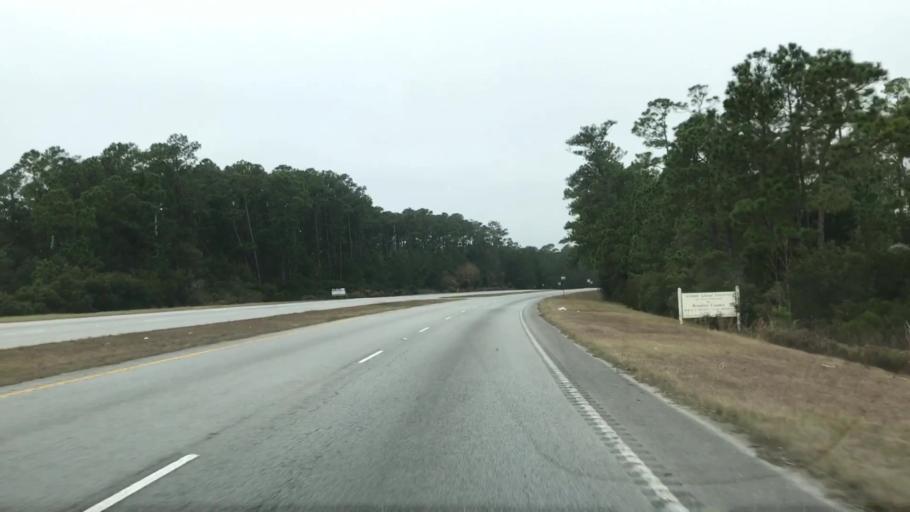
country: US
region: South Carolina
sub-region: Beaufort County
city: Shell Point
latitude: 32.3694
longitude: -80.8119
